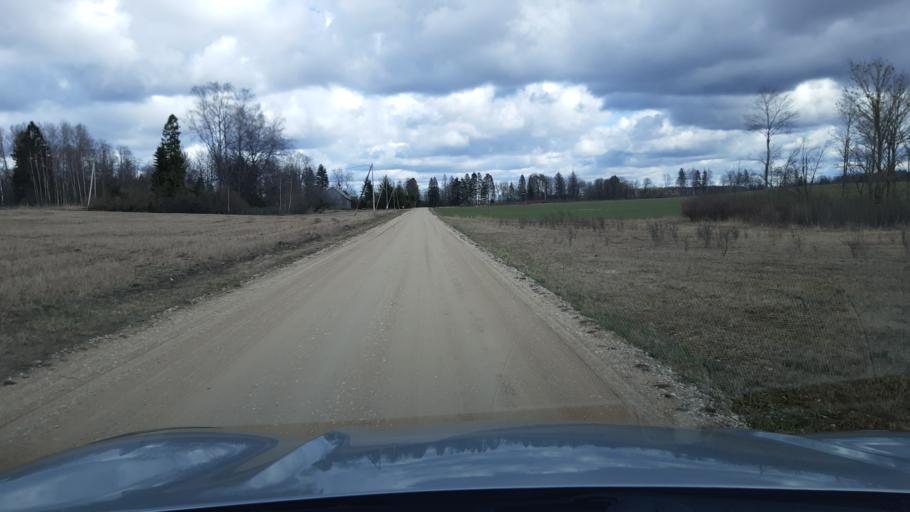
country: EE
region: Harju
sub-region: Rae vald
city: Vaida
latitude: 59.0775
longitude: 25.1144
